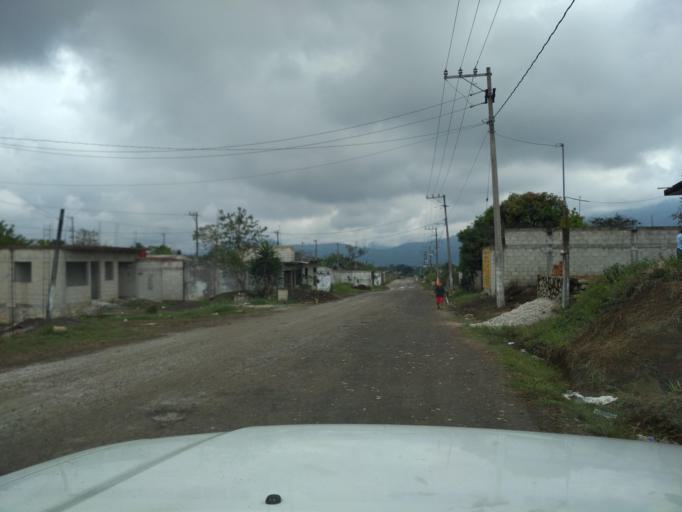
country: MX
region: Veracruz
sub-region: Cordoba
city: San Jose de Tapia
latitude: 18.8502
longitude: -96.9687
